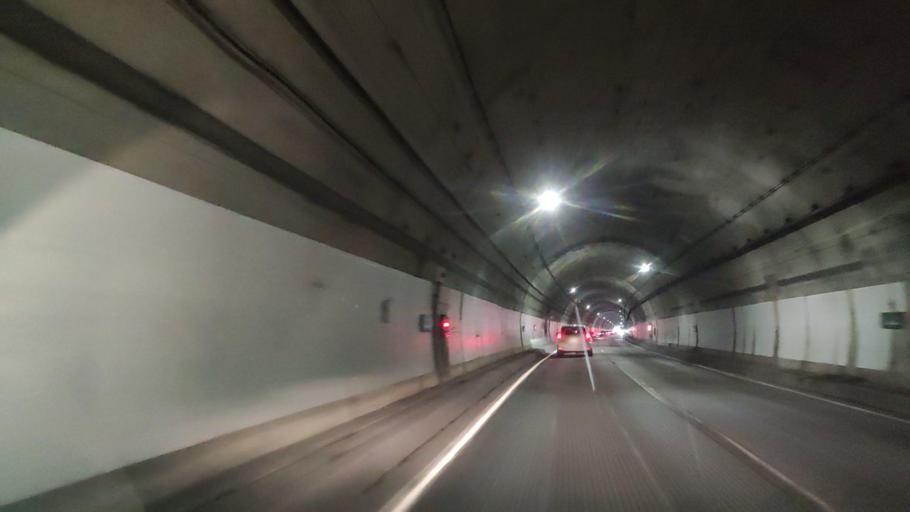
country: JP
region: Hokkaido
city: Rumoi
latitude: 43.7003
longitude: 141.3377
